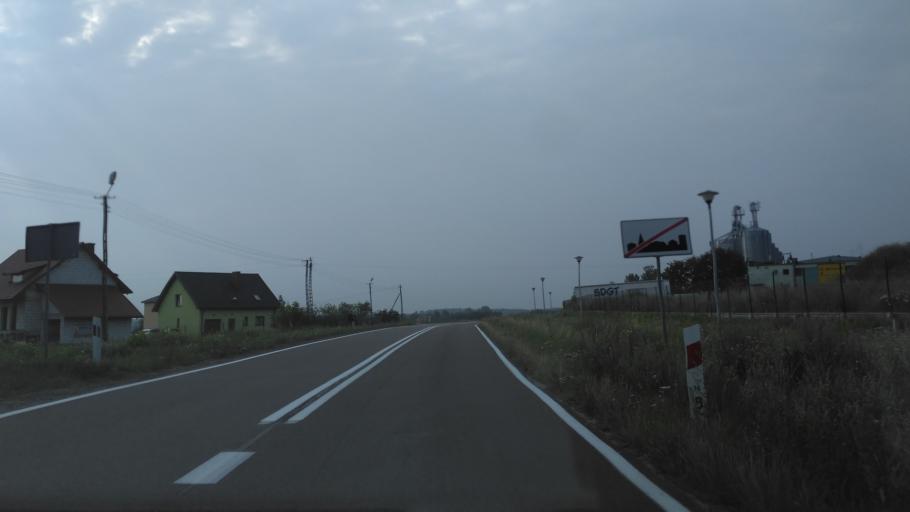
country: PL
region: Lublin Voivodeship
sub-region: Powiat chelmski
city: Rejowiec Fabryczny
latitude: 51.1848
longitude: 23.1722
